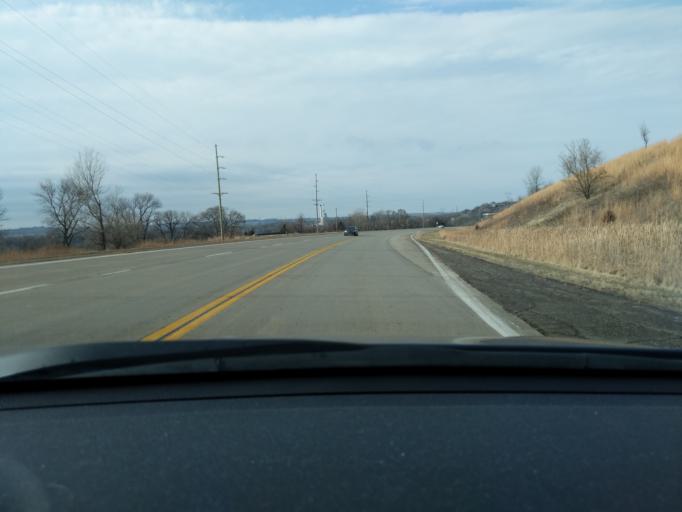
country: US
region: Minnesota
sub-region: Yellow Medicine County
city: Granite Falls
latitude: 44.7970
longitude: -95.5050
